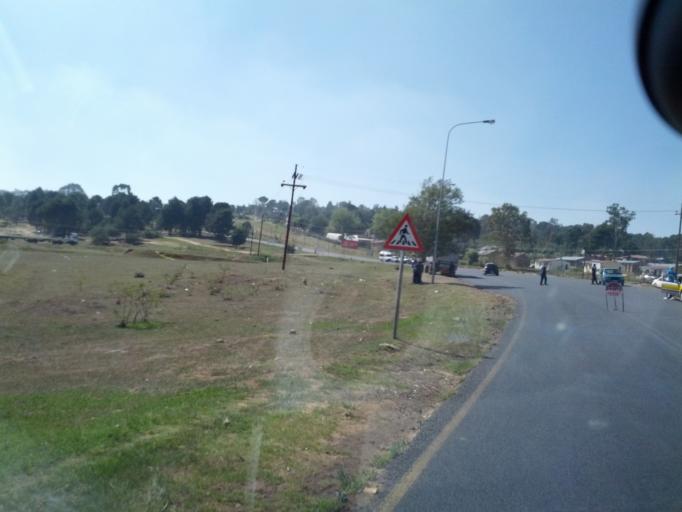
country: LS
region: Berea
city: Teyateyaneng
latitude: -29.1462
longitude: 27.7211
